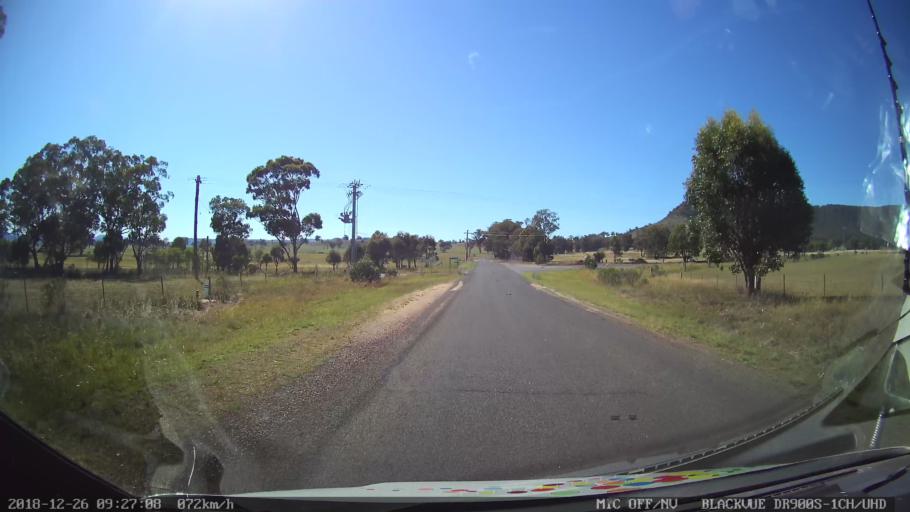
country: AU
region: New South Wales
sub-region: Mid-Western Regional
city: Kandos
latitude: -32.8330
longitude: 150.0149
